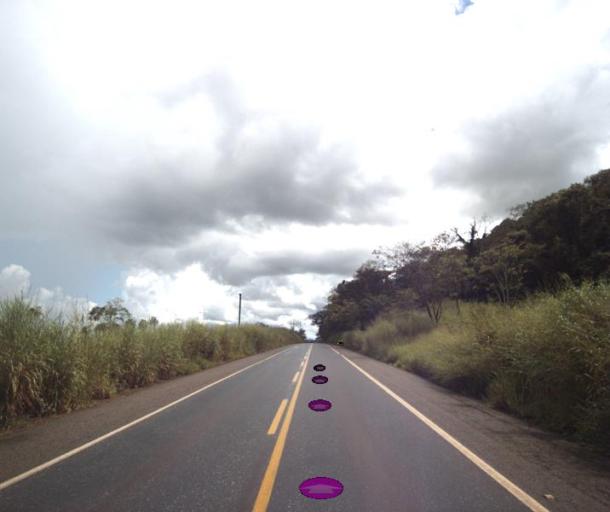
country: BR
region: Goias
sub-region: Pirenopolis
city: Pirenopolis
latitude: -16.0660
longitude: -49.0611
